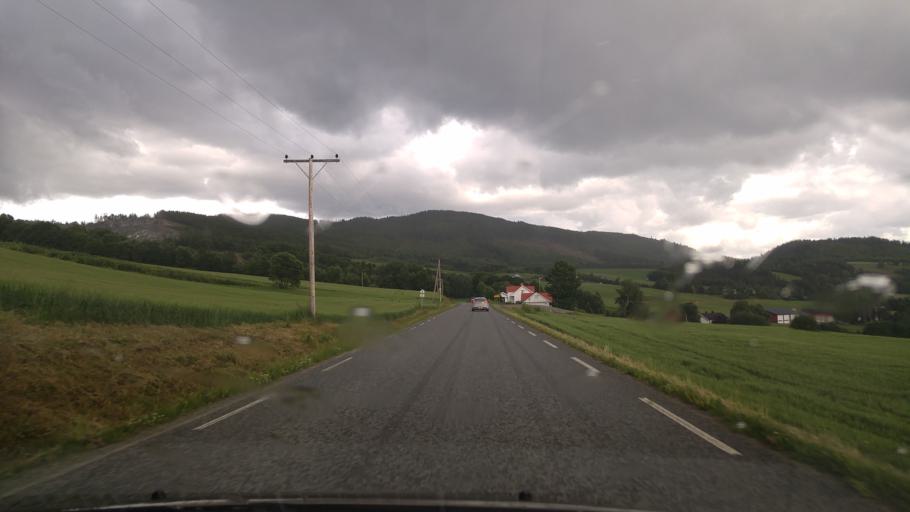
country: NO
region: Nord-Trondelag
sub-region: Levanger
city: Skogn
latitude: 63.6844
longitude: 11.2375
